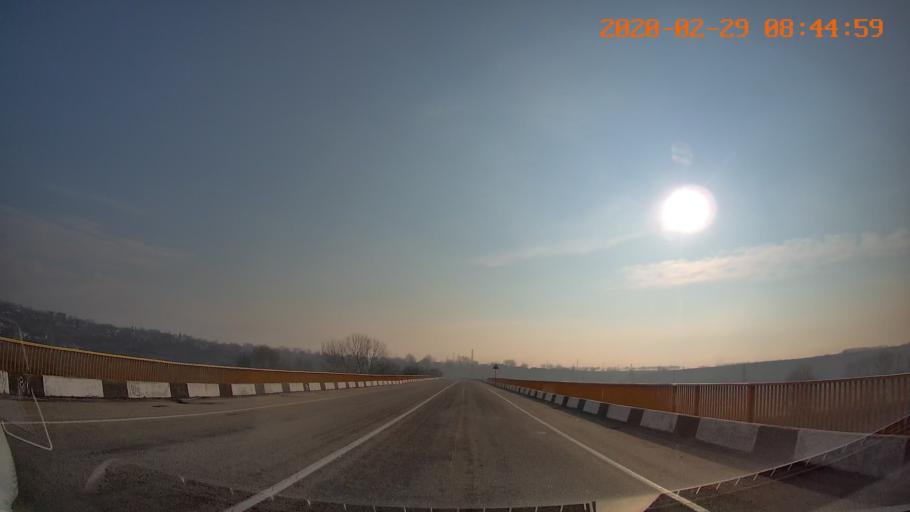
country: MD
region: Anenii Noi
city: Varnita
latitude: 46.9197
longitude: 29.4730
